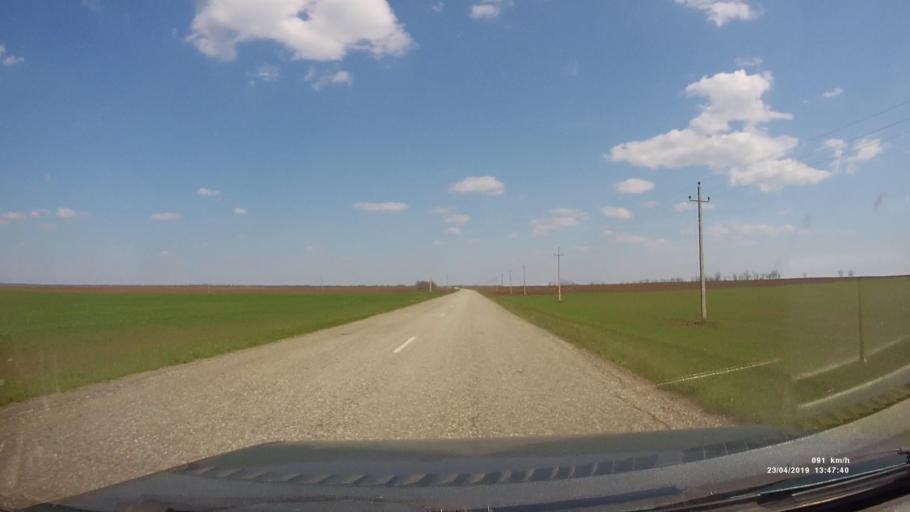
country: RU
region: Kalmykiya
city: Yashalta
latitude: 46.5993
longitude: 42.8582
